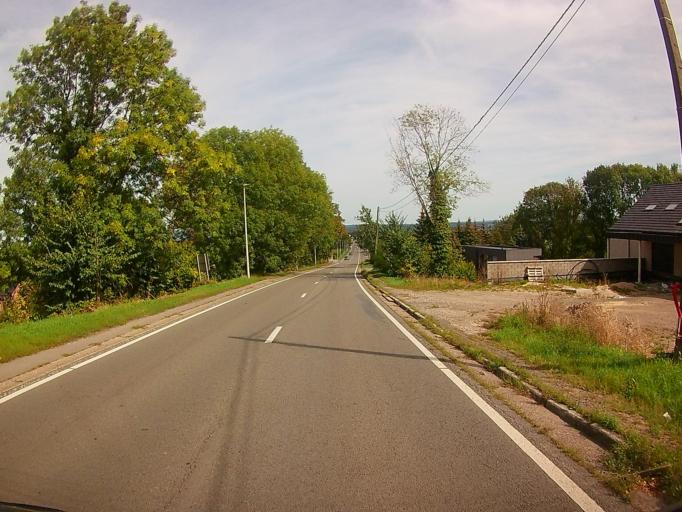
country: BE
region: Wallonia
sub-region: Province de Liege
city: Welkenraedt
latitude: 50.6811
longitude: 5.9427
